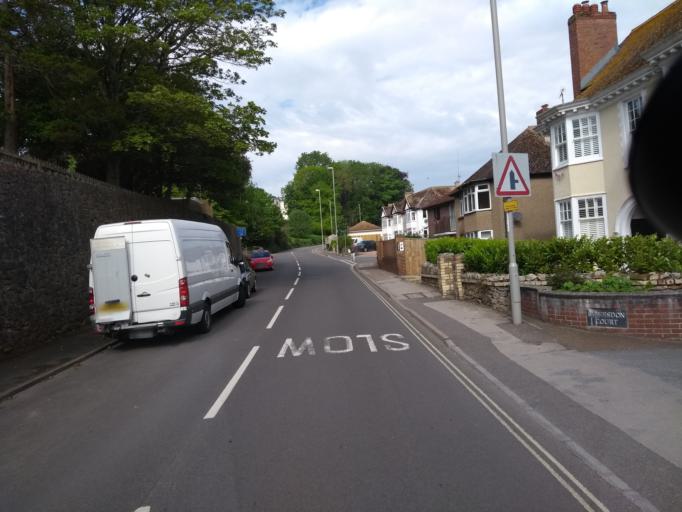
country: GB
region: England
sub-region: Dorset
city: Lyme Regis
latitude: 50.7273
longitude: -2.9412
